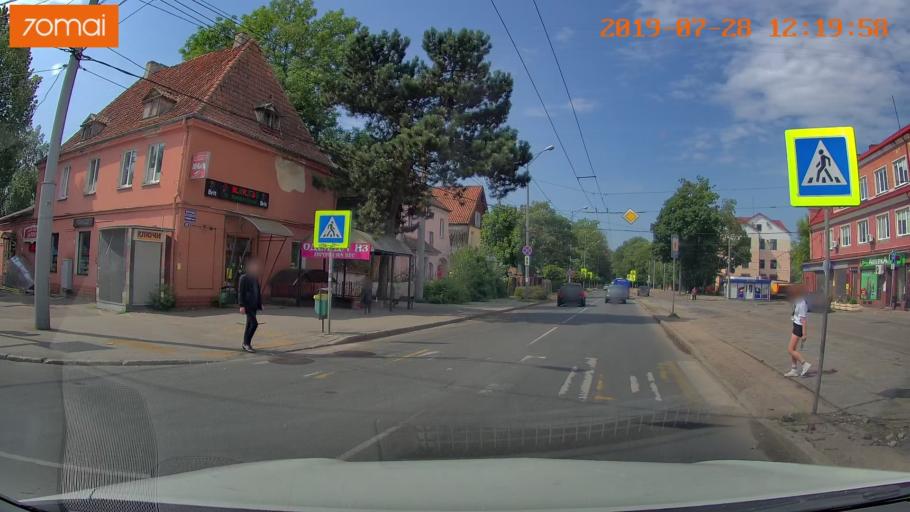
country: RU
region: Kaliningrad
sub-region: Gorod Kaliningrad
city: Kaliningrad
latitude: 54.7143
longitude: 20.4580
